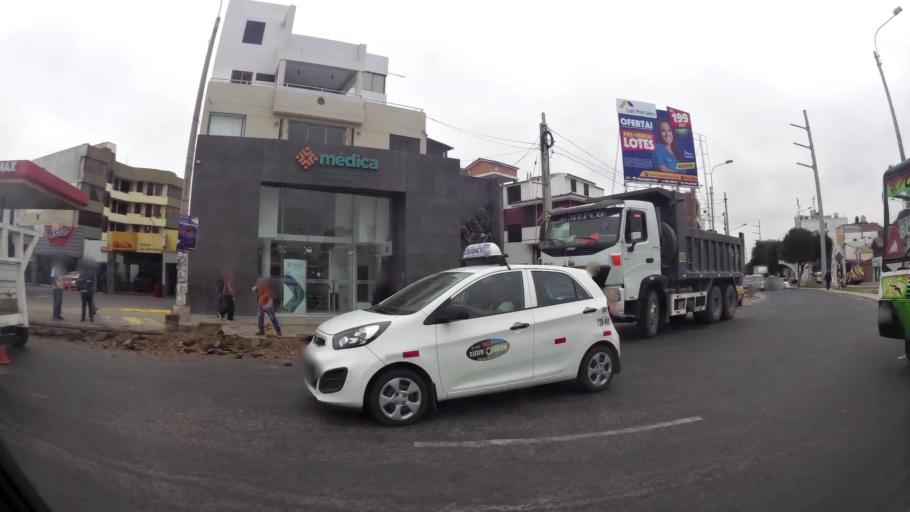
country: PE
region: La Libertad
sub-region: Provincia de Trujillo
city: Trujillo
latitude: -8.1244
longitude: -79.0391
